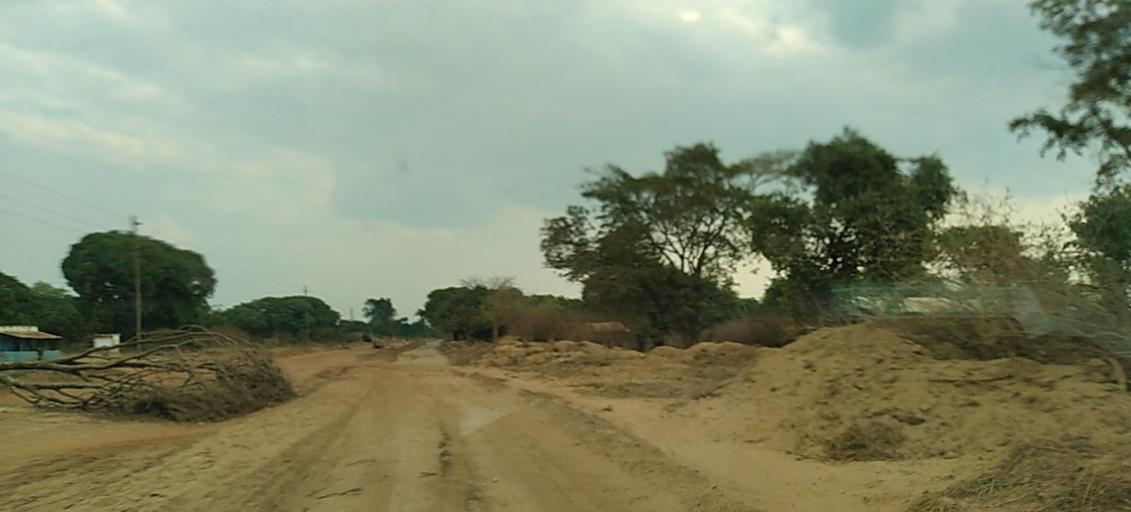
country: ZM
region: Copperbelt
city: Kalulushi
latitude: -12.8958
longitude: 27.9498
